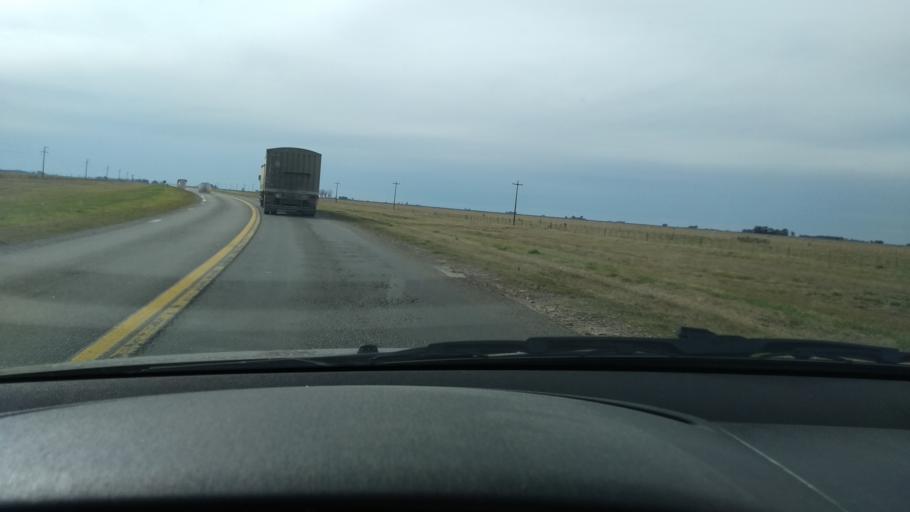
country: AR
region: Buenos Aires
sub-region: Partido de Azul
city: Azul
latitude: -36.7166
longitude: -59.7631
